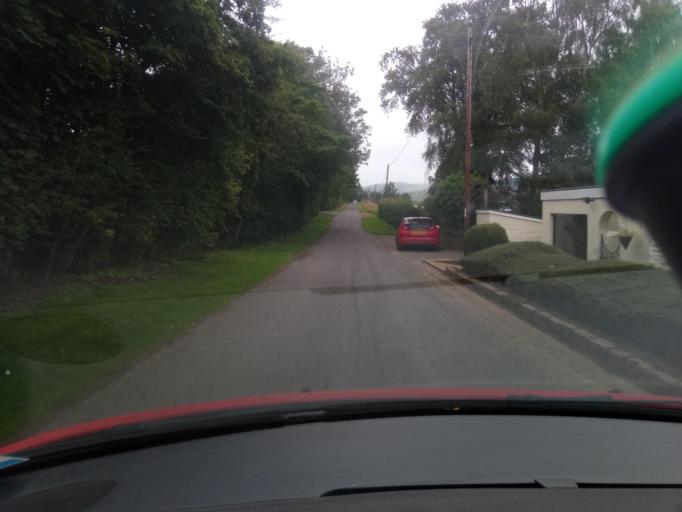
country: GB
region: Scotland
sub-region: The Scottish Borders
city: Galashiels
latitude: 55.7219
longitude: -2.8963
